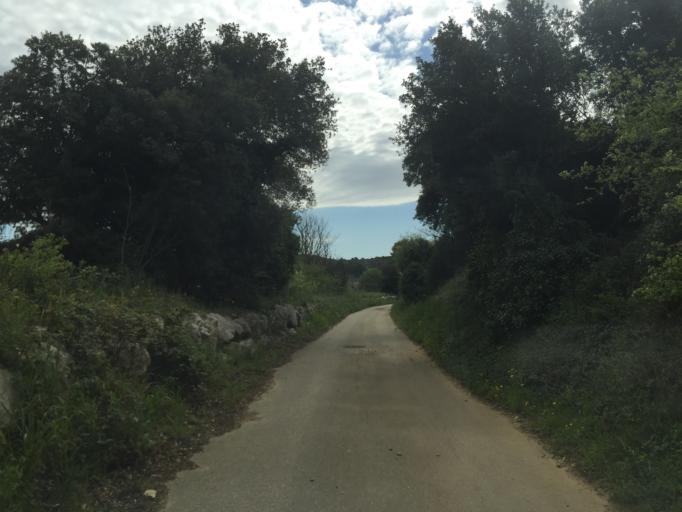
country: FR
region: Provence-Alpes-Cote d'Azur
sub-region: Departement du Vaucluse
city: Chateauneuf-du-Pape
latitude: 44.0755
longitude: 4.8255
